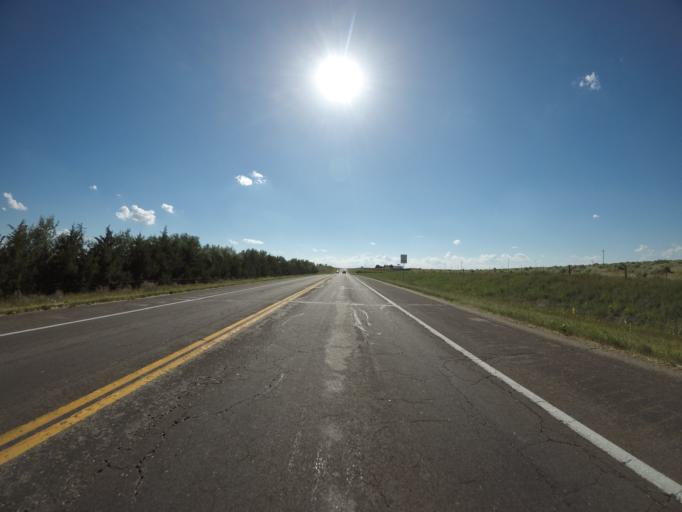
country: US
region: Colorado
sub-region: Logan County
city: Sterling
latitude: 40.6239
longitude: -103.3127
